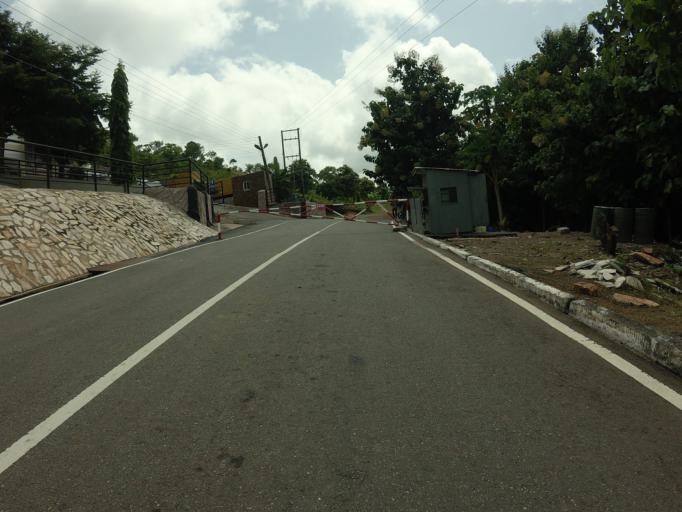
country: GH
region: Volta
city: Ho
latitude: 6.6145
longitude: 0.4551
